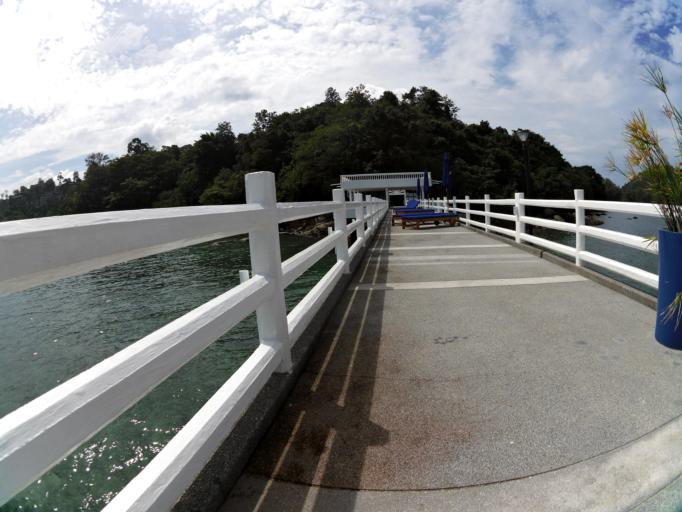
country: TH
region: Phuket
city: Patong
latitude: 7.8890
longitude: 98.2812
